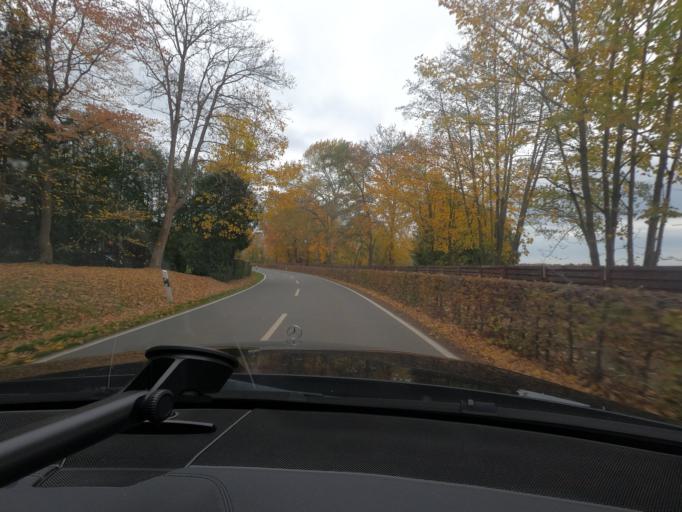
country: DE
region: North Rhine-Westphalia
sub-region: Regierungsbezirk Arnsberg
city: Mohnesee
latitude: 51.4866
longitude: 8.1475
